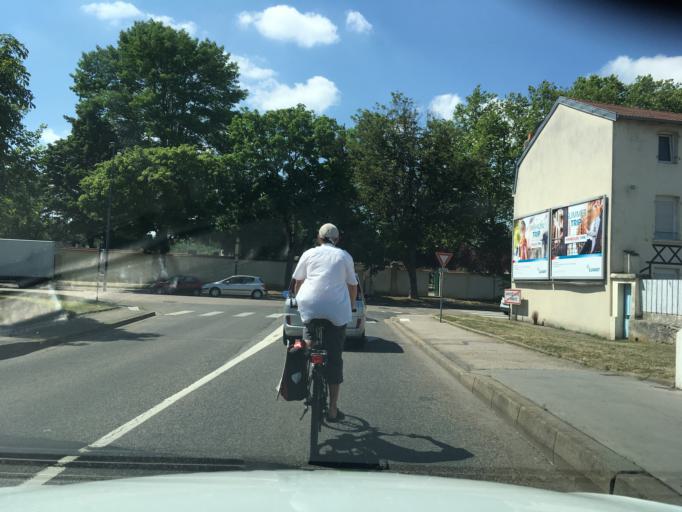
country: FR
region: Lorraine
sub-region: Departement de Meurthe-et-Moselle
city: Jarville-la-Malgrange
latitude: 48.6720
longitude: 6.1940
